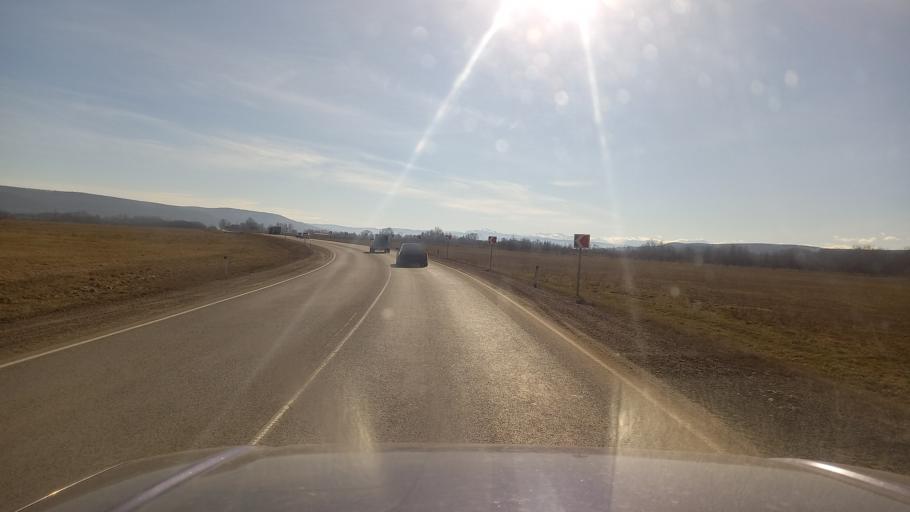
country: RU
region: Adygeya
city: Tul'skiy
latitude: 44.5217
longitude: 40.1357
